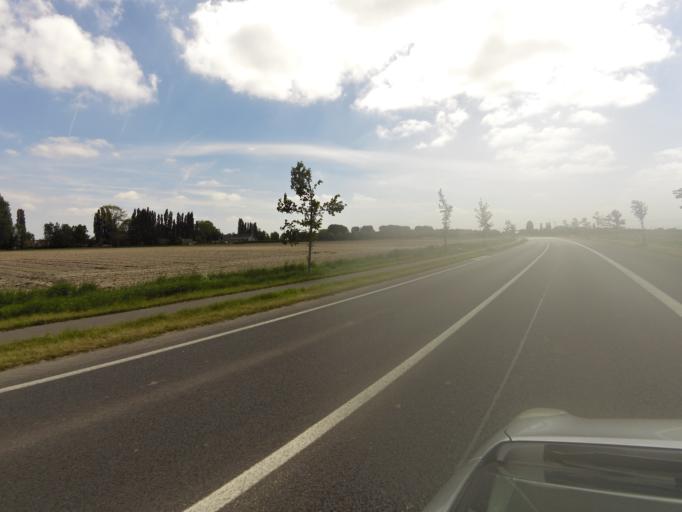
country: BE
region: Flanders
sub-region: Provincie West-Vlaanderen
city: Diksmuide
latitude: 51.0770
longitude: 2.8745
